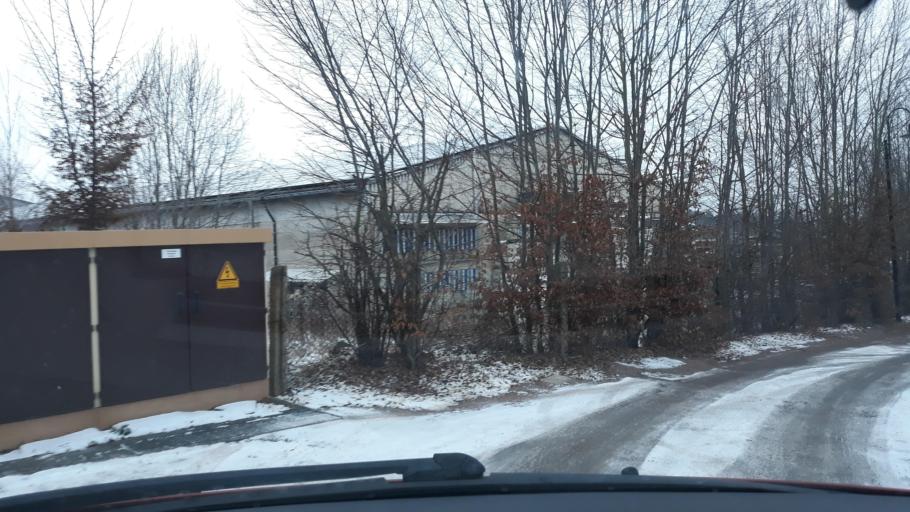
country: DE
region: Saxony
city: Kirchberg
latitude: 50.6167
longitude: 12.4960
